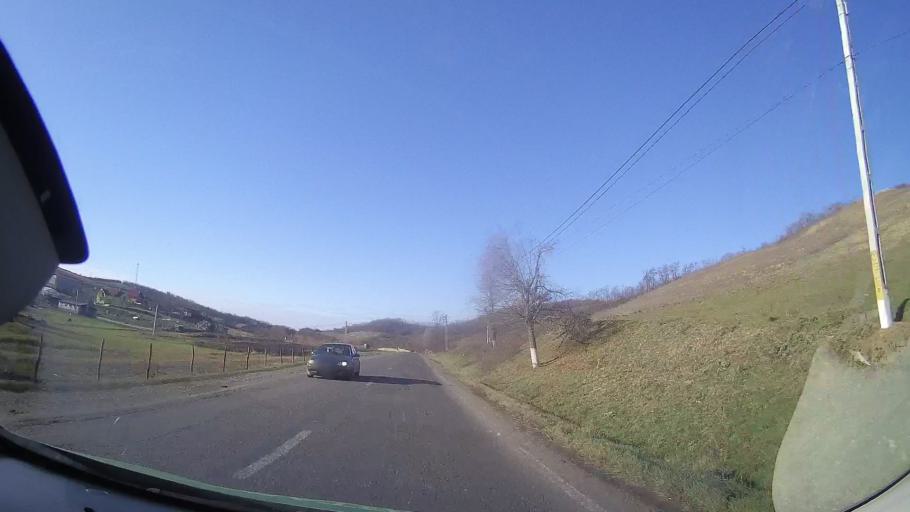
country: RO
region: Mures
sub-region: Comuna Sarmasu
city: Sarmasu
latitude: 46.7899
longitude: 24.1939
